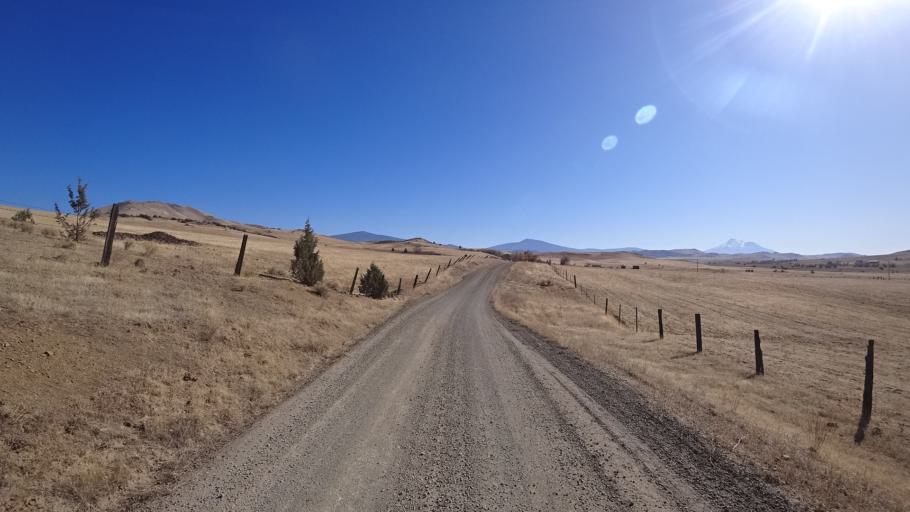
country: US
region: California
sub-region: Siskiyou County
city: Montague
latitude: 41.8467
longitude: -122.4464
